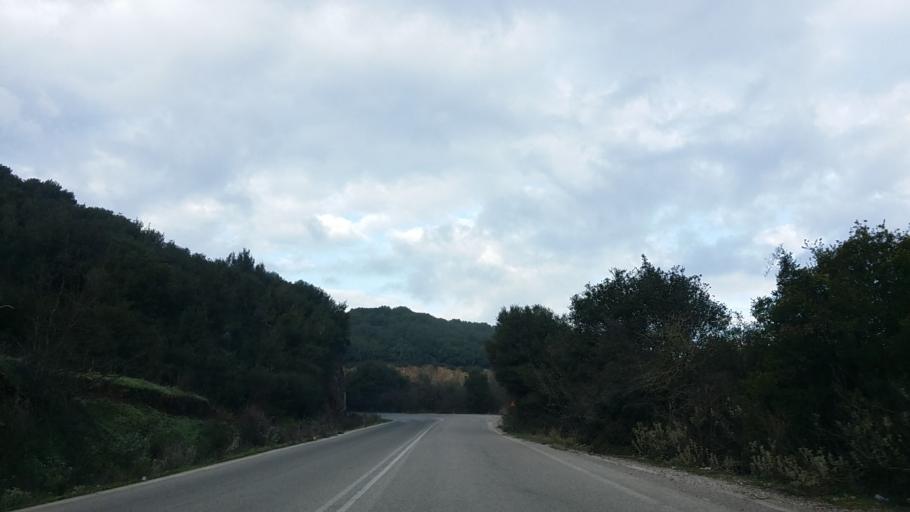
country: GR
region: West Greece
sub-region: Nomos Aitolias kai Akarnanias
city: Katouna
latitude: 38.7781
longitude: 21.1261
